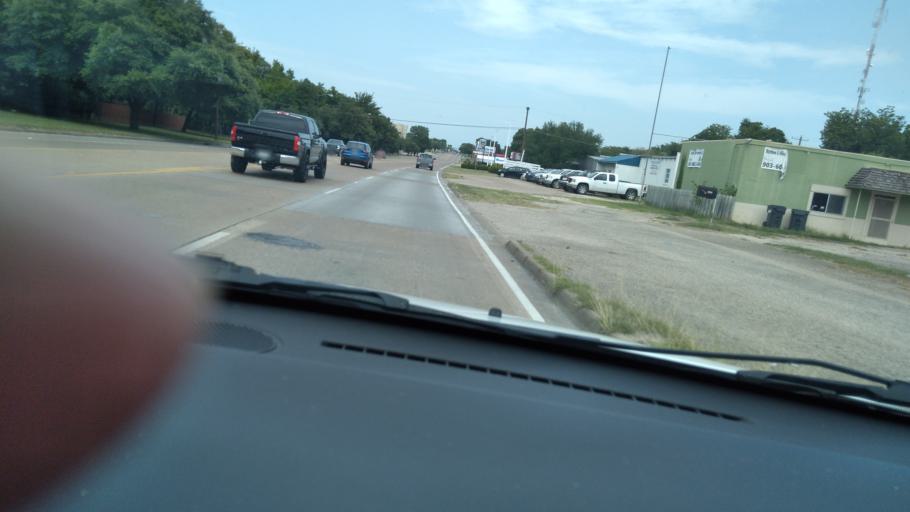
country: US
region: Texas
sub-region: Navarro County
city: Corsicana
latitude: 32.0765
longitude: -96.4948
